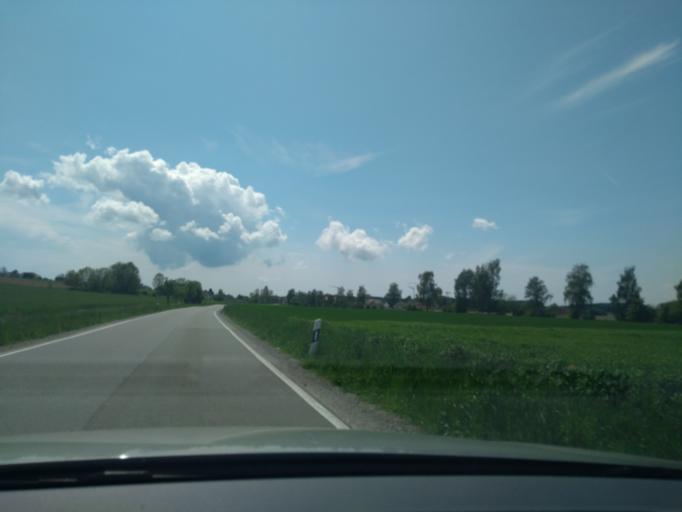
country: DE
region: Baden-Wuerttemberg
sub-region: Tuebingen Region
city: Bad Waldsee
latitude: 47.9285
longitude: 9.8078
